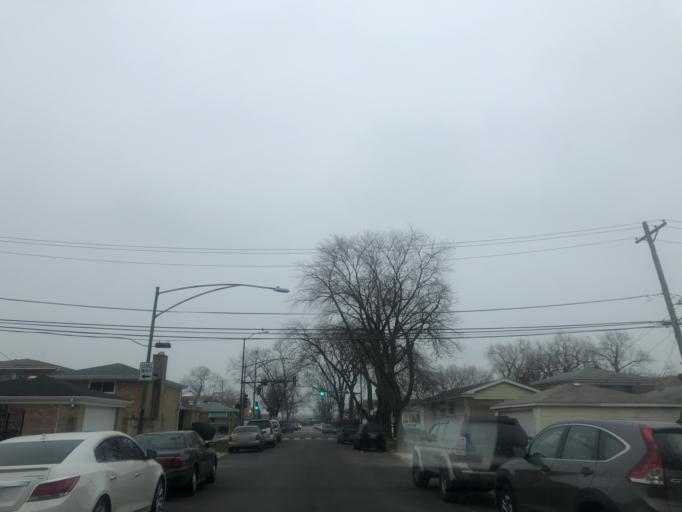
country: US
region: Illinois
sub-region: Cook County
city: Evergreen Park
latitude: 41.7443
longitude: -87.6281
